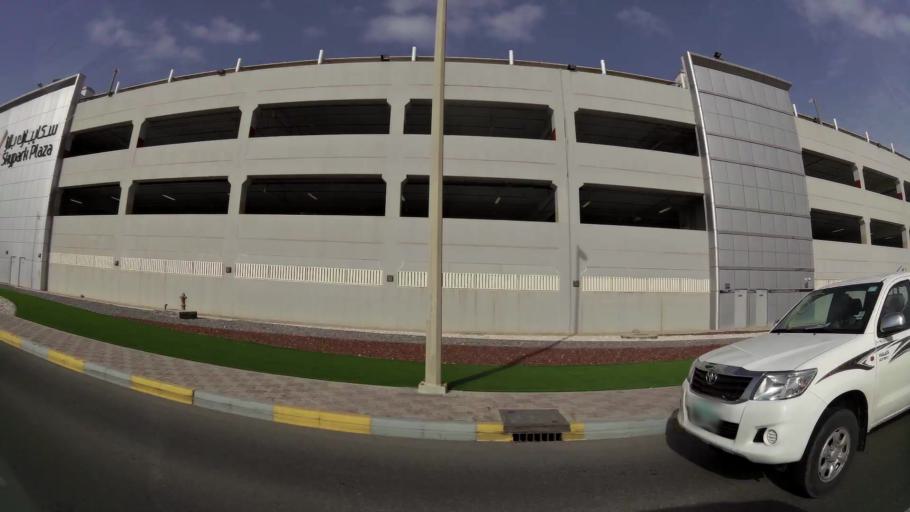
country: AE
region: Abu Dhabi
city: Abu Dhabi
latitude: 24.4275
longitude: 54.6422
